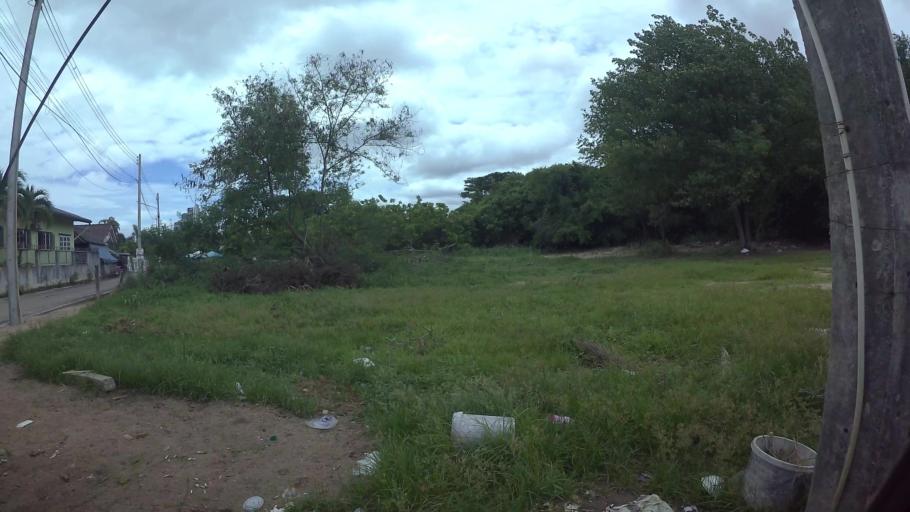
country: TH
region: Chon Buri
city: Sattahip
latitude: 12.7642
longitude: 100.8983
